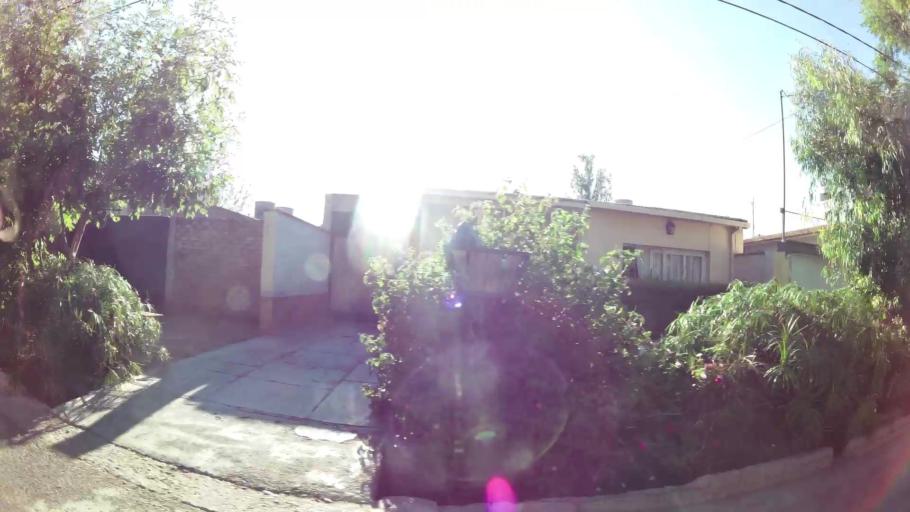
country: AR
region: Mendoza
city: Las Heras
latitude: -32.8563
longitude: -68.8194
